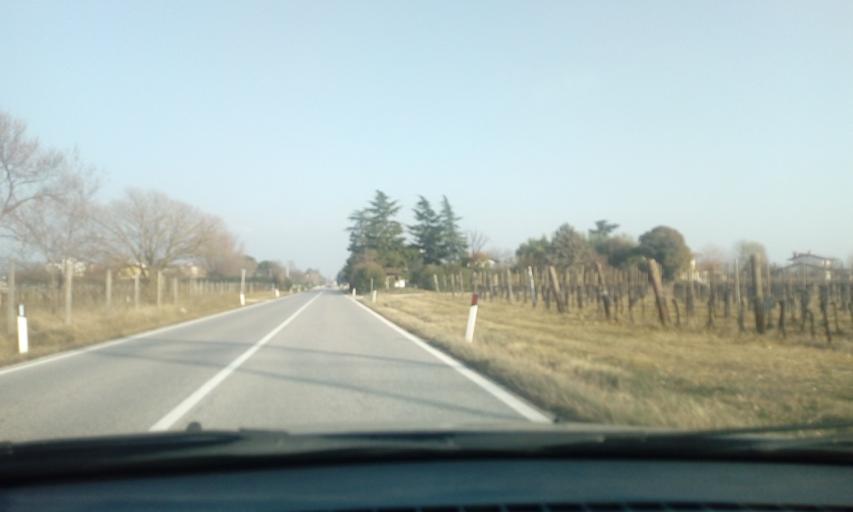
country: IT
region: Friuli Venezia Giulia
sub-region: Provincia di Gorizia
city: Cormons
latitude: 45.9527
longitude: 13.4534
